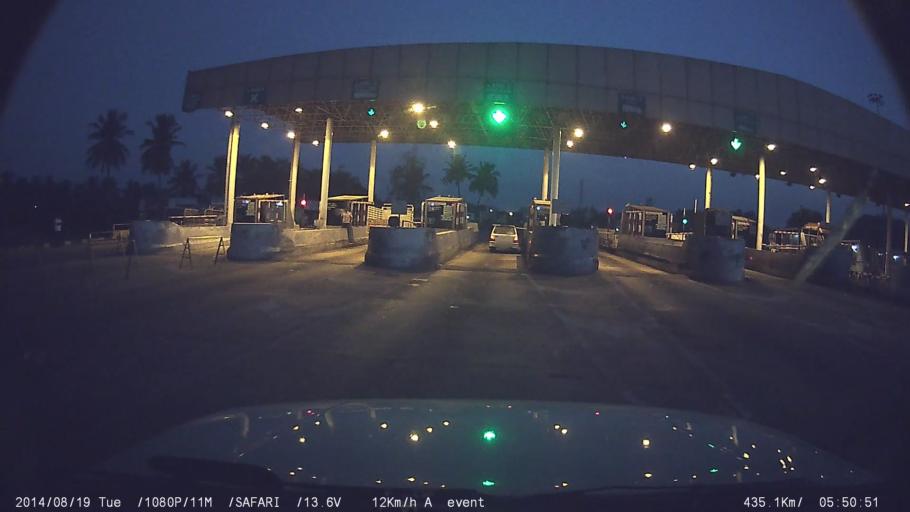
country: IN
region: Tamil Nadu
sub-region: Salem
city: Omalur
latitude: 11.7197
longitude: 78.0737
